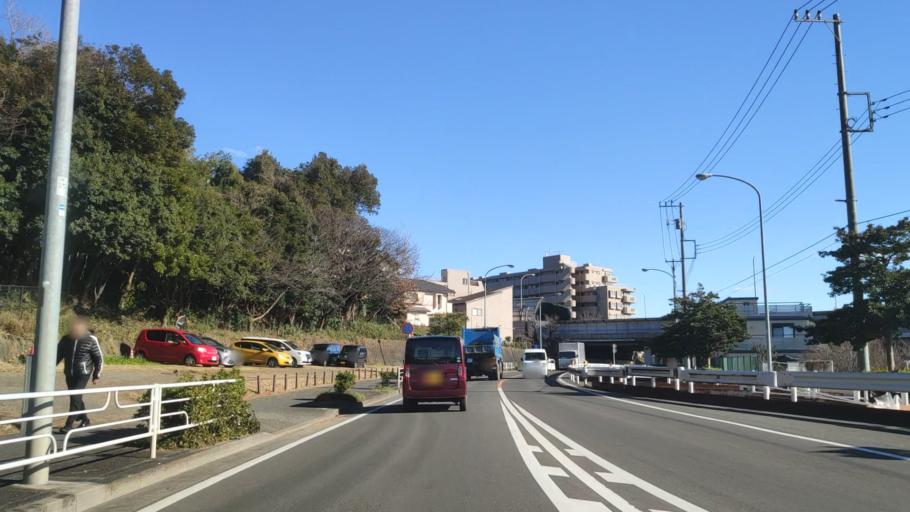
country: JP
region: Tokyo
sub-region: Machida-shi
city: Machida
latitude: 35.5312
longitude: 139.5189
